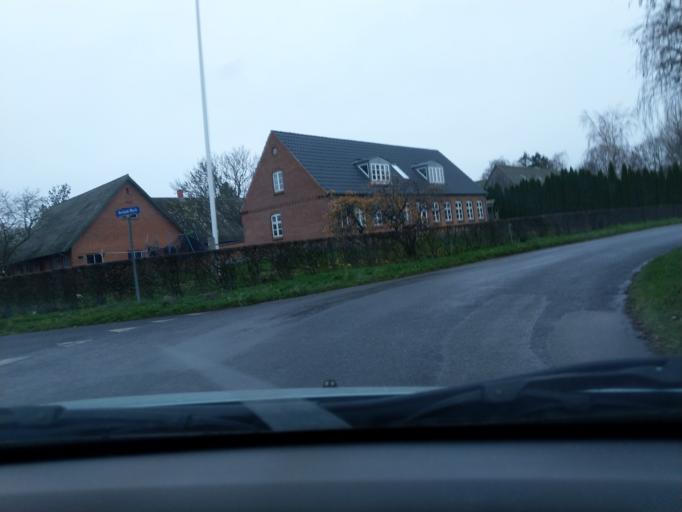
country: DK
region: Zealand
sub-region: Vordingborg Kommune
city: Praesto
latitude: 55.1109
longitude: 12.1064
